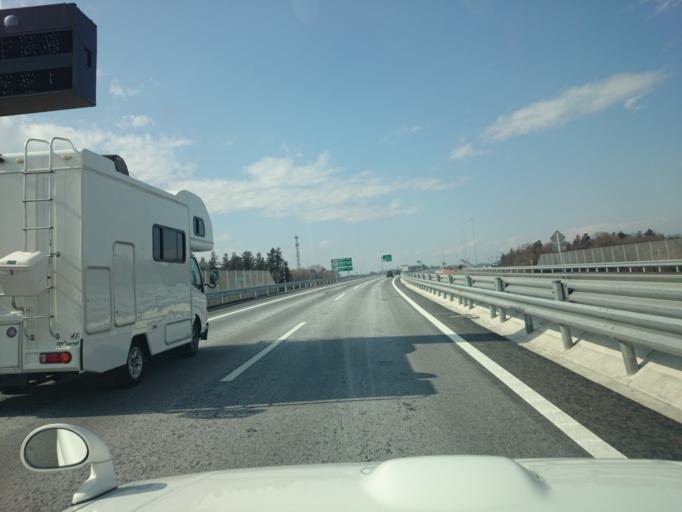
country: JP
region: Ibaraki
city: Sakai
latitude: 36.1242
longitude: 139.8115
